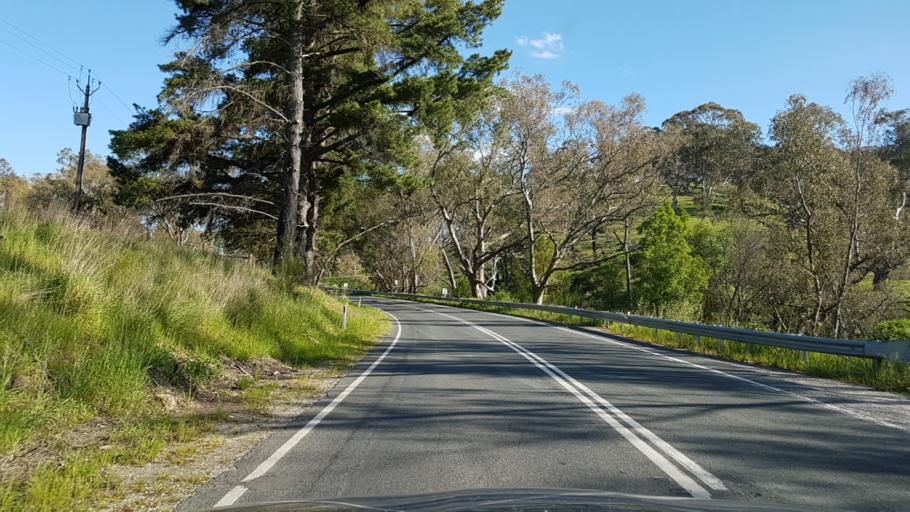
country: AU
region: South Australia
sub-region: Adelaide Hills
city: Gumeracha
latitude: -34.8317
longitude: 138.8910
